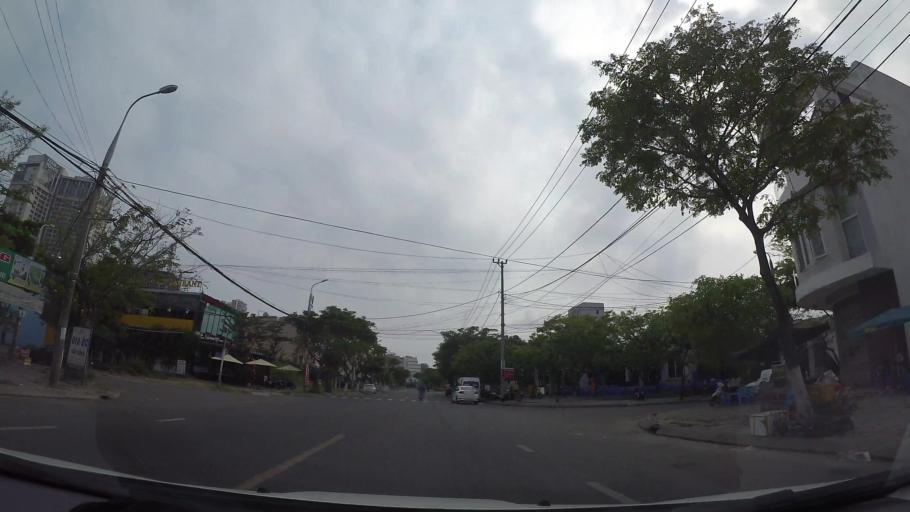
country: VN
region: Da Nang
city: Son Tra
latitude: 16.0806
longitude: 108.2437
